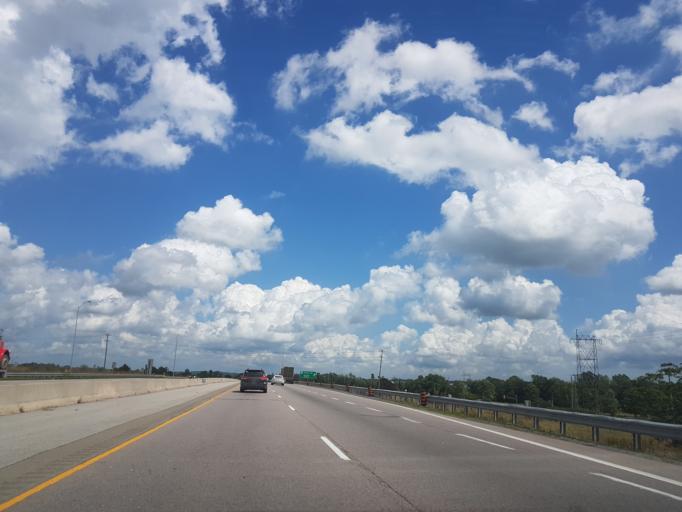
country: CA
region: Ontario
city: Greater Napanee
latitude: 44.2637
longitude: -76.9679
